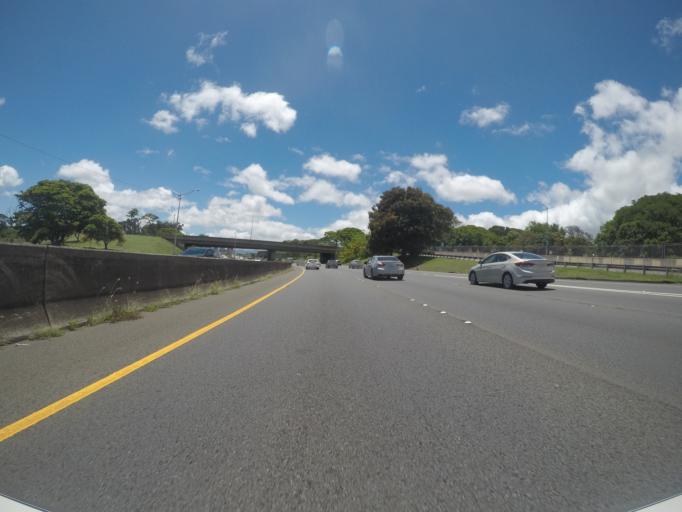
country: US
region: Hawaii
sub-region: Honolulu County
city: Halawa Heights
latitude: 21.3421
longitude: -157.8871
